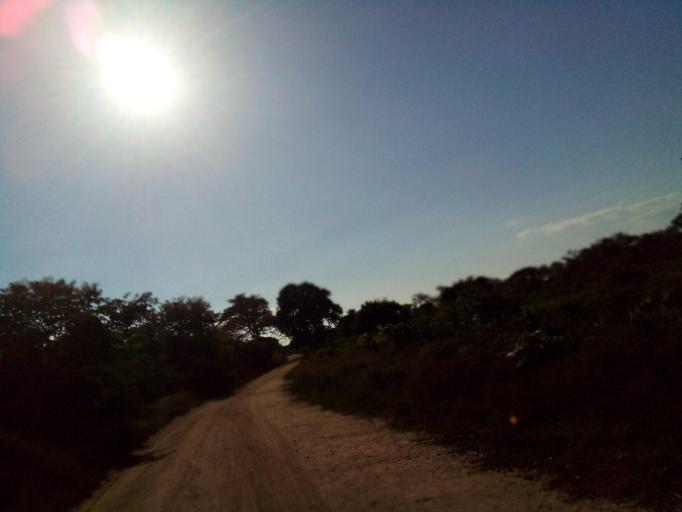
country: MZ
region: Zambezia
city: Quelimane
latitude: -17.4918
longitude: 36.5671
